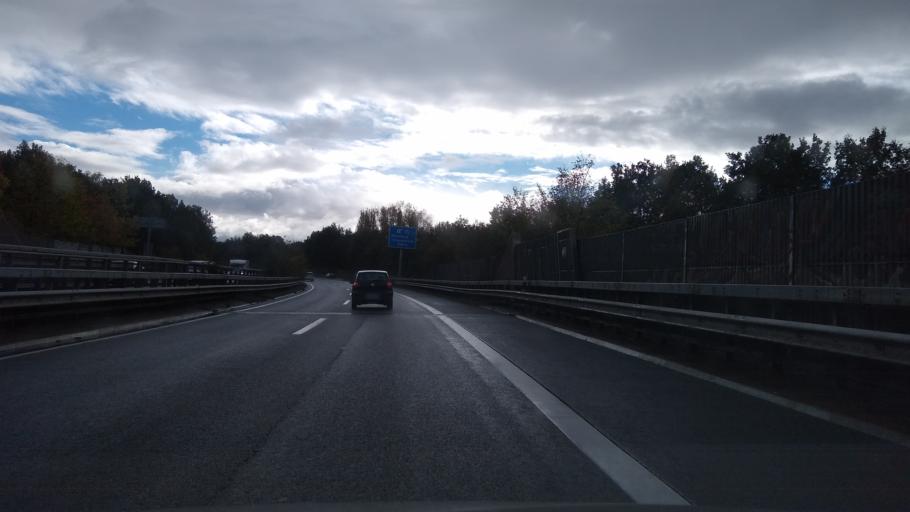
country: DE
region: Lower Saxony
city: Oldenburg
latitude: 53.1306
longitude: 8.1952
